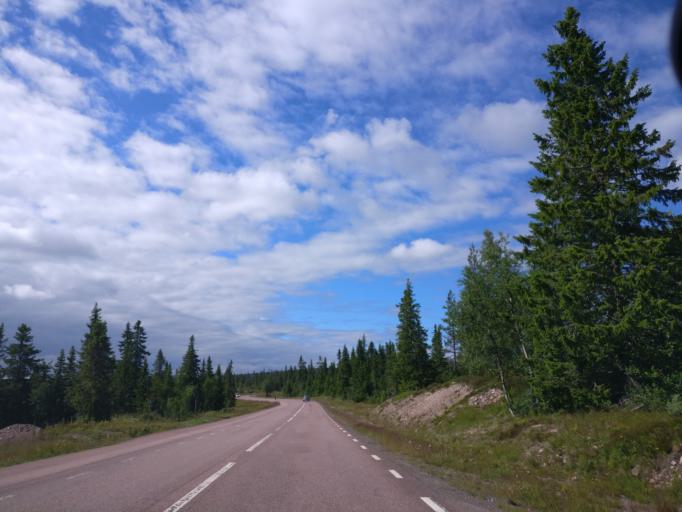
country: SE
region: Dalarna
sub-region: Malung-Saelens kommun
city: Malung
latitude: 61.1609
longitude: 13.1103
